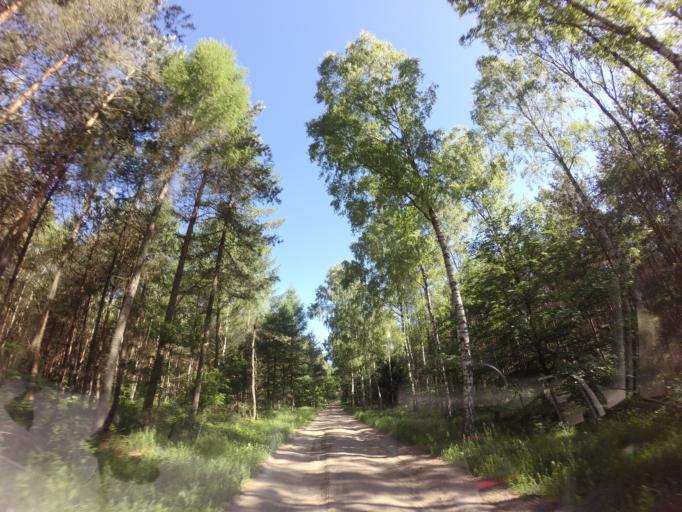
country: PL
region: West Pomeranian Voivodeship
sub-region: Powiat choszczenski
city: Drawno
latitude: 53.2312
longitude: 15.6727
